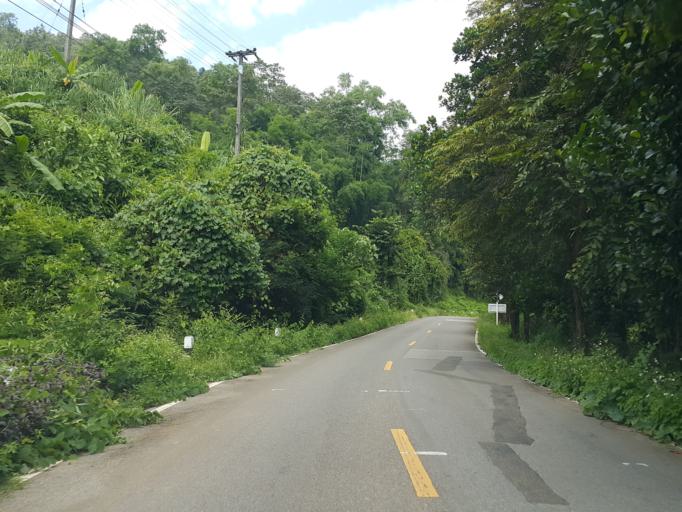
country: TH
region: Mae Hong Son
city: Mae Hong Son
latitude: 19.4805
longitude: 97.9638
